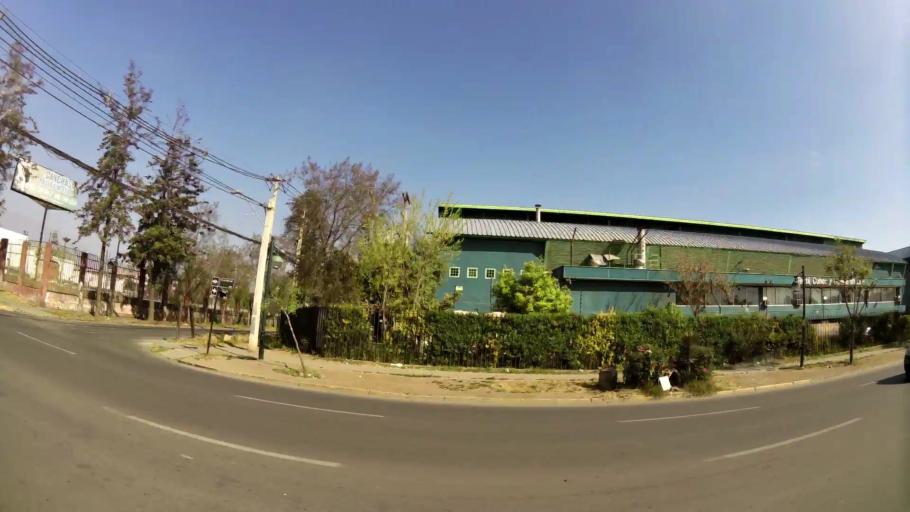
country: CL
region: Santiago Metropolitan
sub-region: Provincia de Santiago
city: Santiago
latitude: -33.4711
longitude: -70.6203
